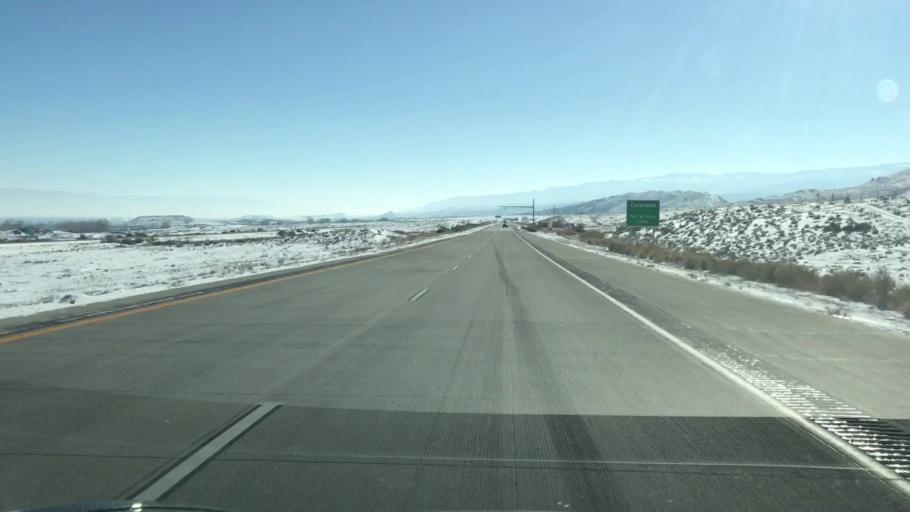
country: US
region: Colorado
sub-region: Mesa County
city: Loma
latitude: 39.1874
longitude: -108.8364
